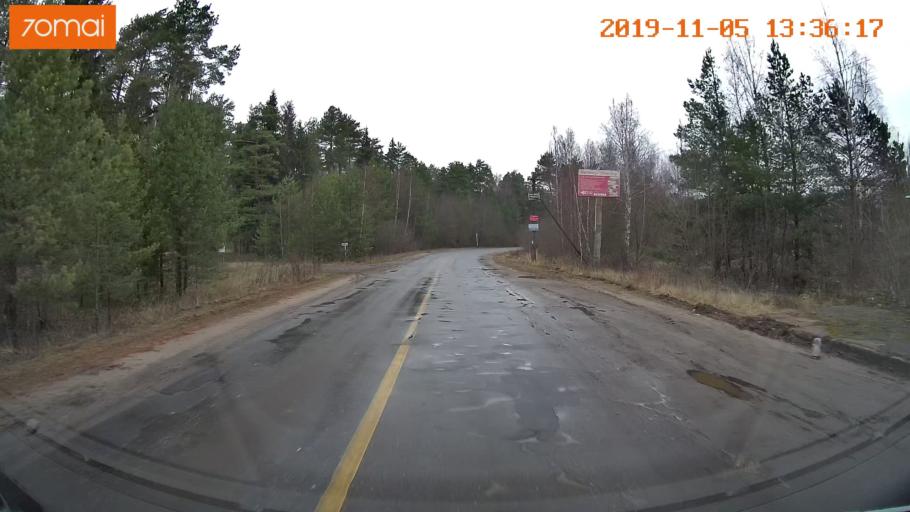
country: RU
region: Ivanovo
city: Shuya
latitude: 56.9136
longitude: 41.3829
